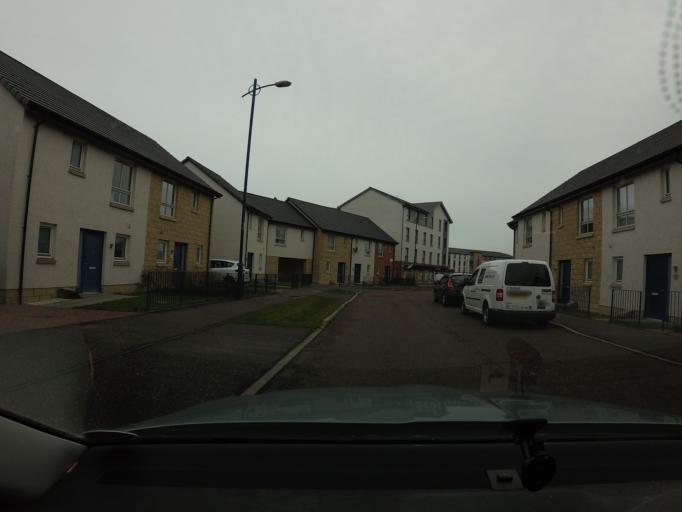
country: GB
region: Scotland
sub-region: South Lanarkshire
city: Rutherglen
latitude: 55.8403
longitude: -4.2385
